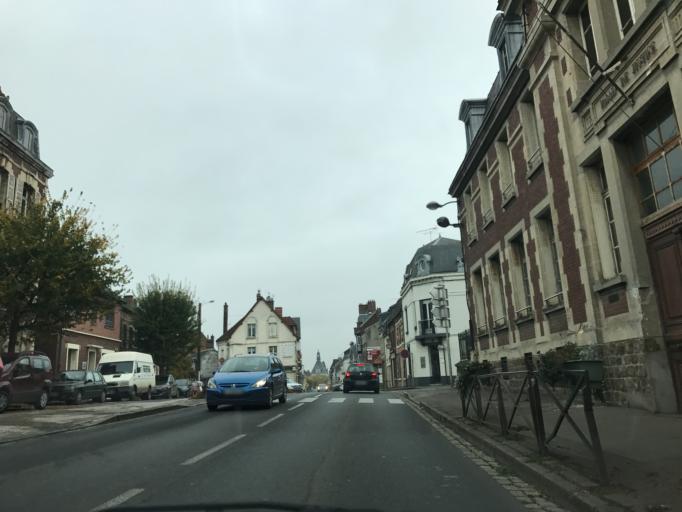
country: FR
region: Picardie
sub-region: Departement de la Somme
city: Peronne
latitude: 49.9267
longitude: 2.9315
